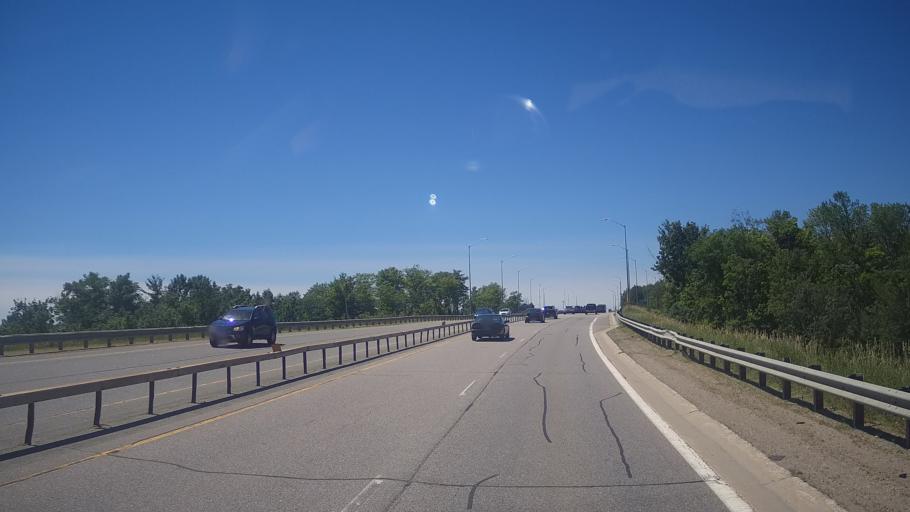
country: CA
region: Ontario
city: Orillia
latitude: 44.6461
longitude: -79.4196
